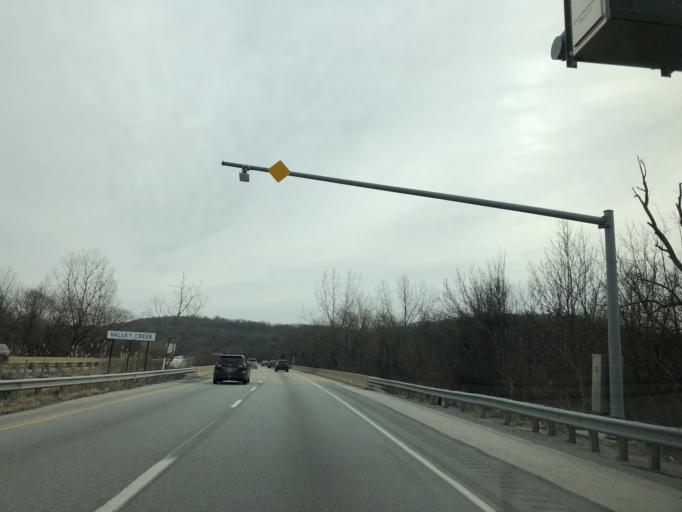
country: US
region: Pennsylvania
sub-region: Chester County
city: Exton
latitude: 40.0138
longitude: -75.6548
